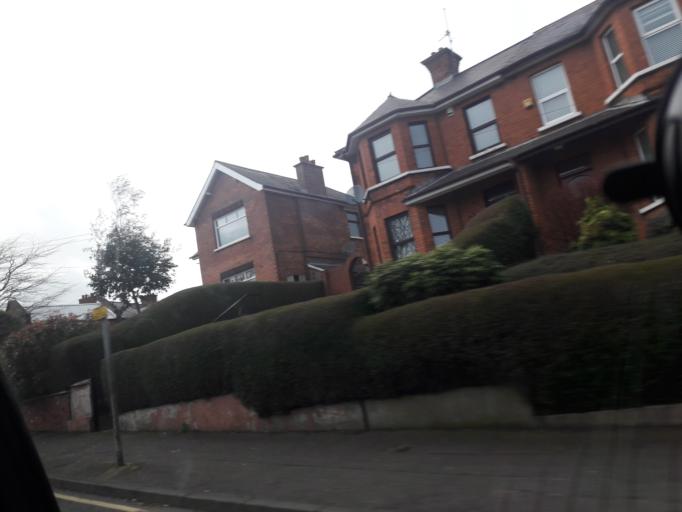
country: GB
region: Northern Ireland
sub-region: City of Belfast
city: Belfast
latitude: 54.6218
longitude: -5.9538
